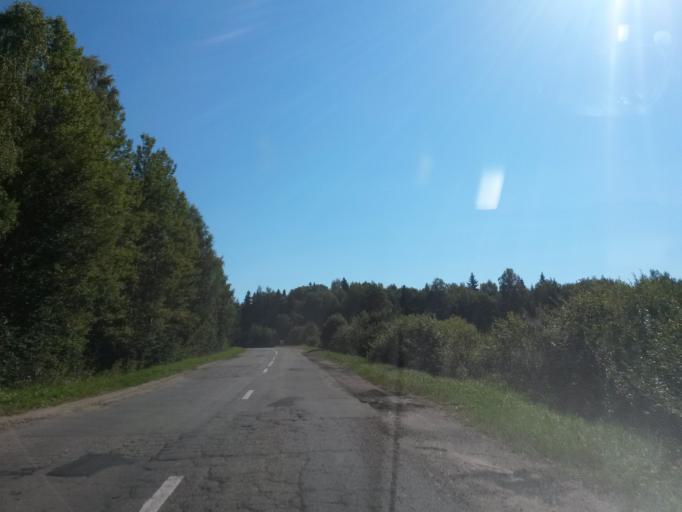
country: RU
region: Jaroslavl
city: Gavrilov-Yam
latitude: 57.2992
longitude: 40.0477
